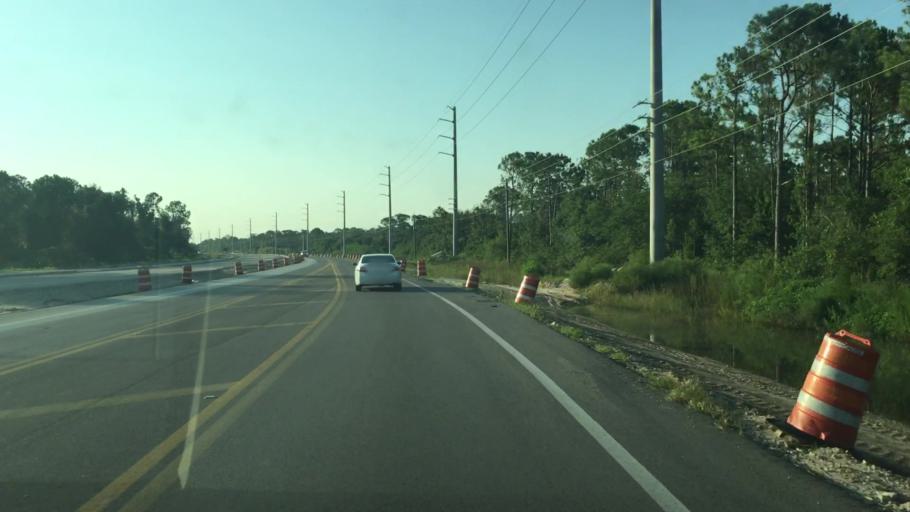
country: US
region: Florida
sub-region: Lee County
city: Gateway
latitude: 26.5931
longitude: -81.7387
